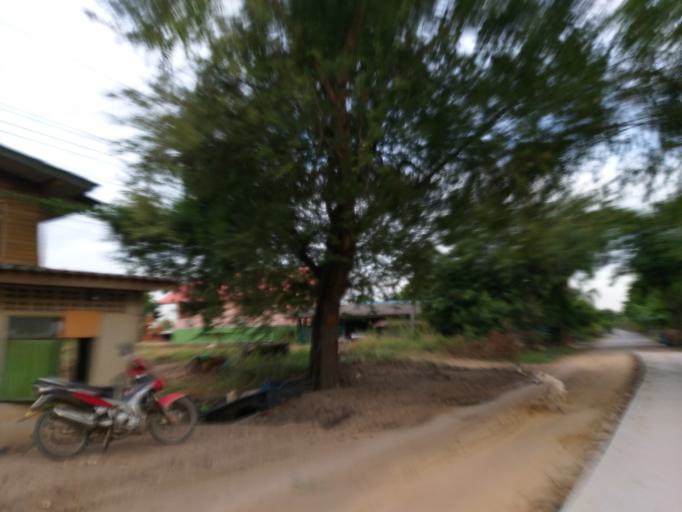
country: TH
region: Pathum Thani
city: Ban Lam Luk Ka
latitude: 14.0140
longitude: 100.7993
